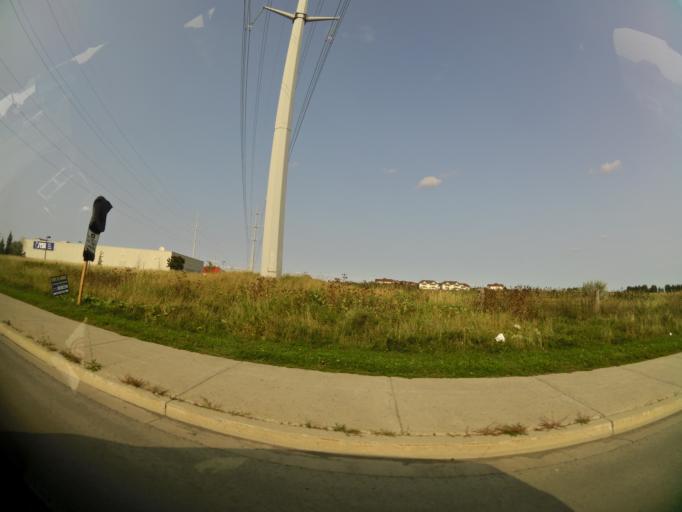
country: CA
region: Ontario
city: Clarence-Rockland
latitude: 45.4572
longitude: -75.4856
